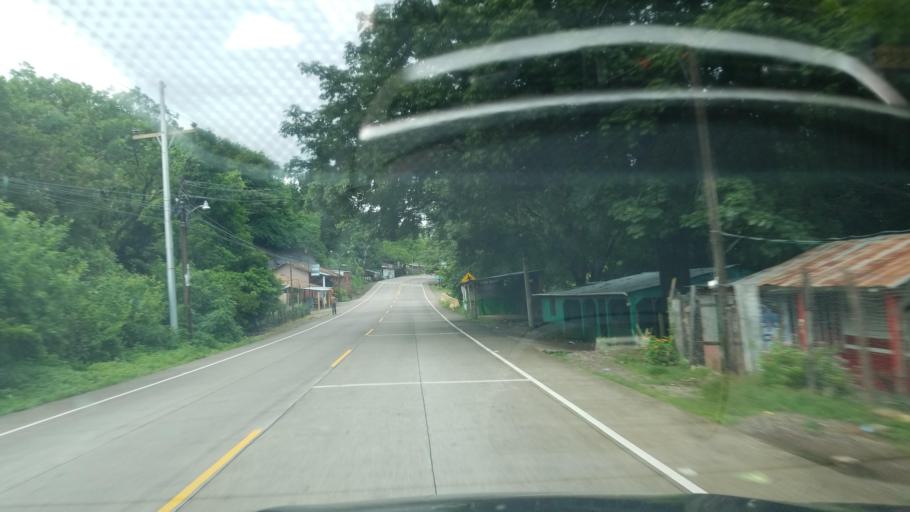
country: HN
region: Choluteca
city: Pespire
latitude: 13.6551
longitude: -87.3652
